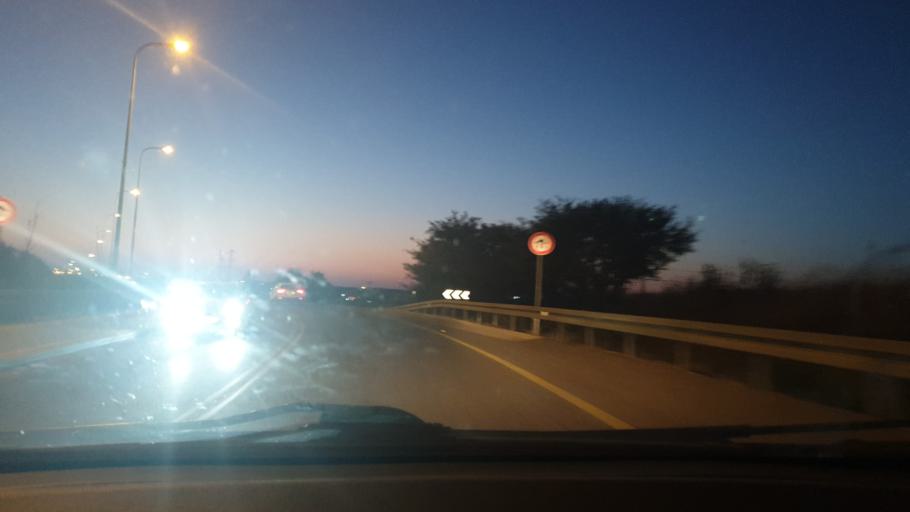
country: IL
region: Central District
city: Bene 'Ayish
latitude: 31.7948
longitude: 34.7646
